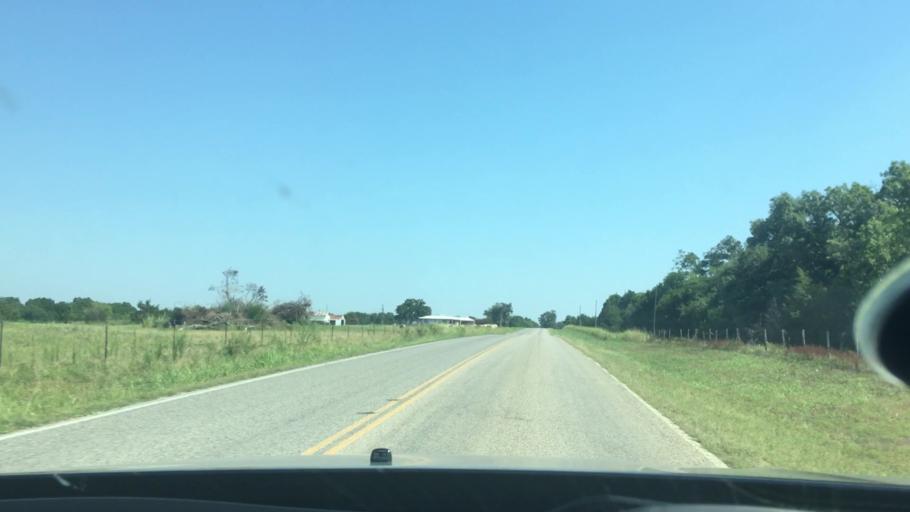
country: US
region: Oklahoma
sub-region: Johnston County
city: Tishomingo
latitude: 34.2758
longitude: -96.6186
